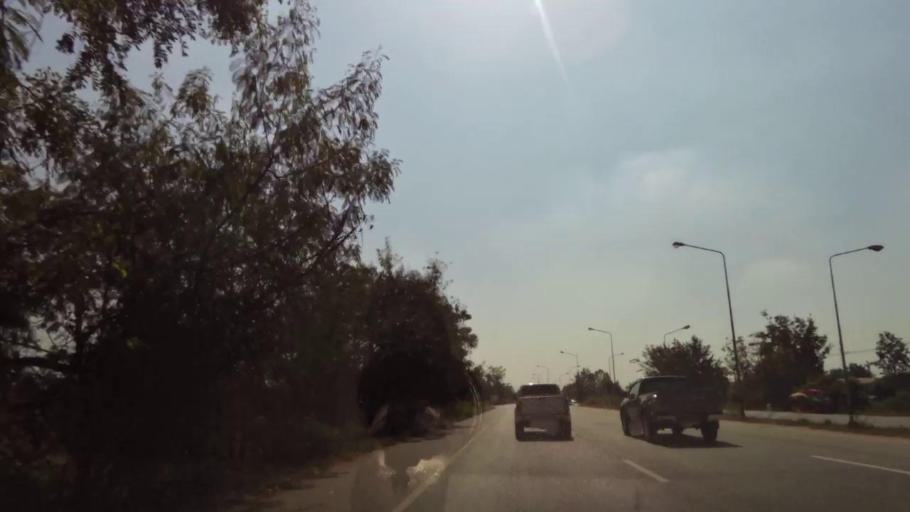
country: TH
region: Phichit
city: Wachira Barami
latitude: 16.4142
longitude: 100.1434
